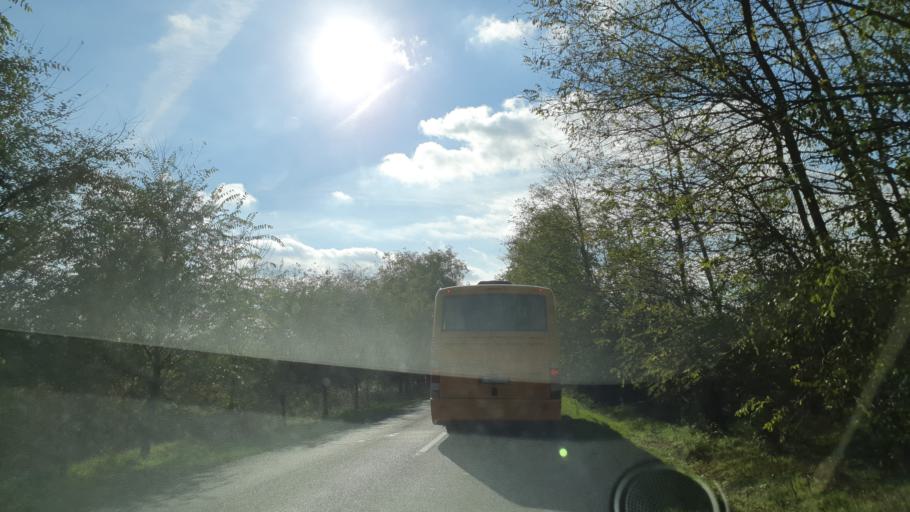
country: HU
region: Szabolcs-Szatmar-Bereg
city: Gyulahaza
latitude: 48.1263
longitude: 22.0885
